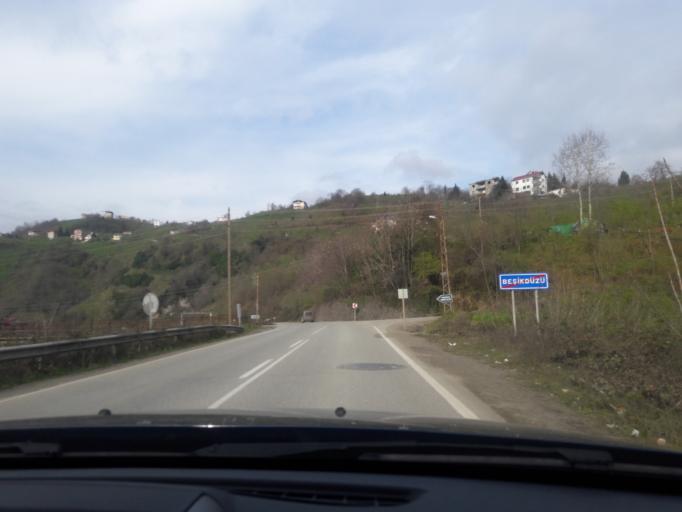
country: TR
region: Trabzon
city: Besikduzu
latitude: 41.0578
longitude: 39.2139
